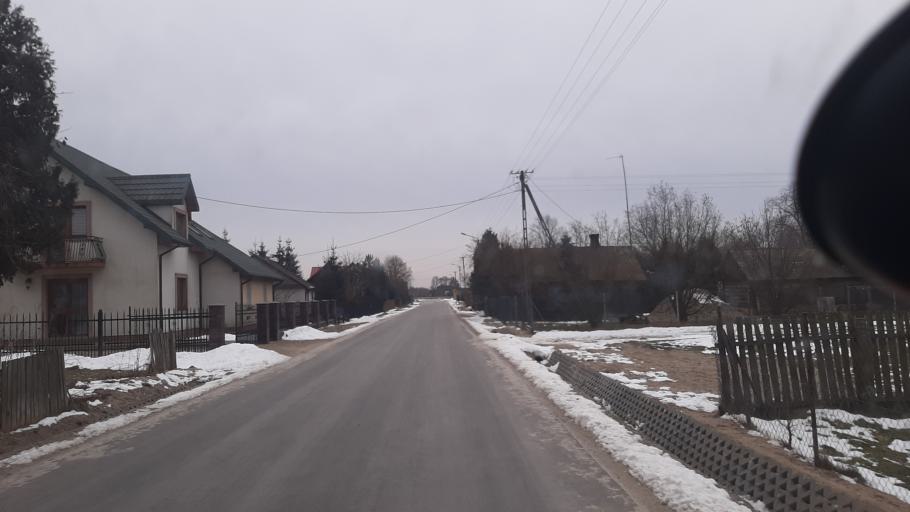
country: PL
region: Lublin Voivodeship
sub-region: Powiat lubartowski
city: Kamionka
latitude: 51.5147
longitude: 22.4725
